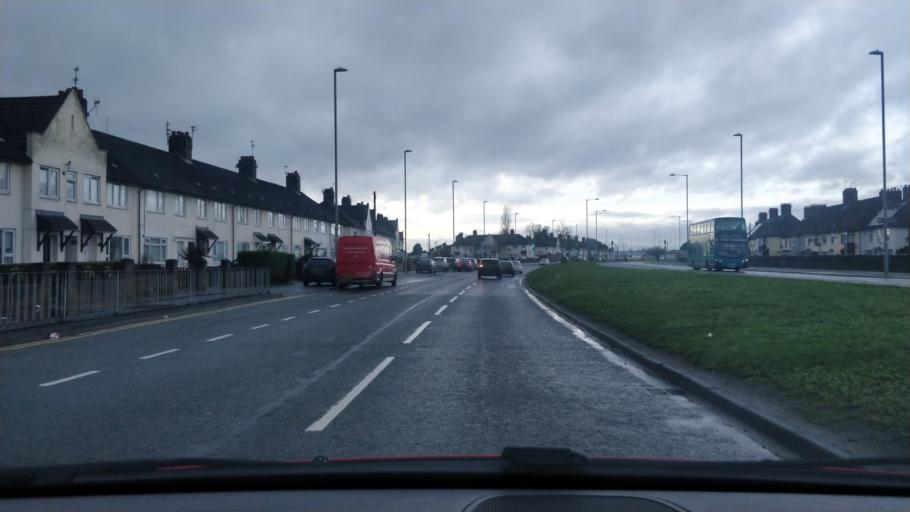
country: GB
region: England
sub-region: Knowsley
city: Huyton
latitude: 53.4204
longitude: -2.8532
